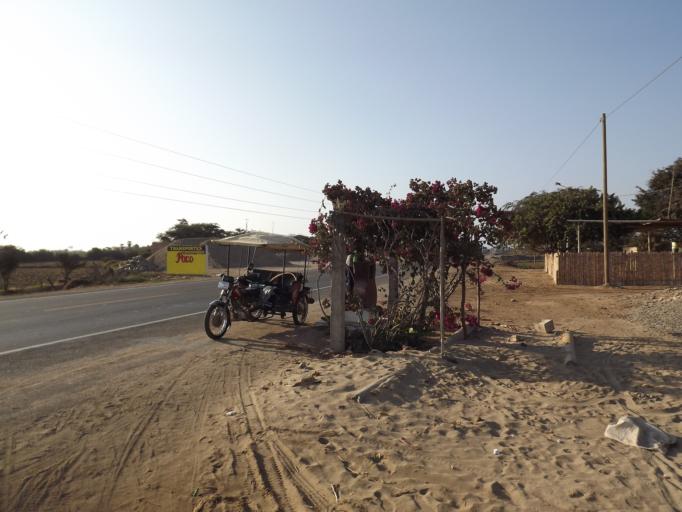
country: PE
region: Lambayeque
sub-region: Provincia de Lambayeque
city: Tucume
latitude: -6.4896
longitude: -79.8575
